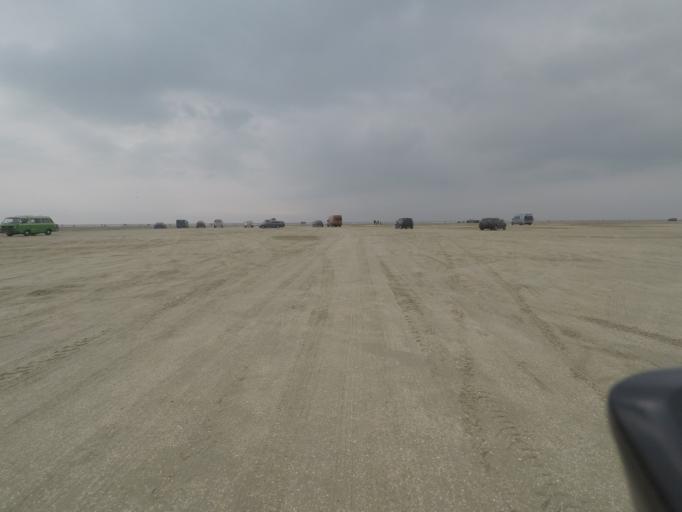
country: DE
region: Schleswig-Holstein
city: List
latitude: 55.1475
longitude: 8.4802
